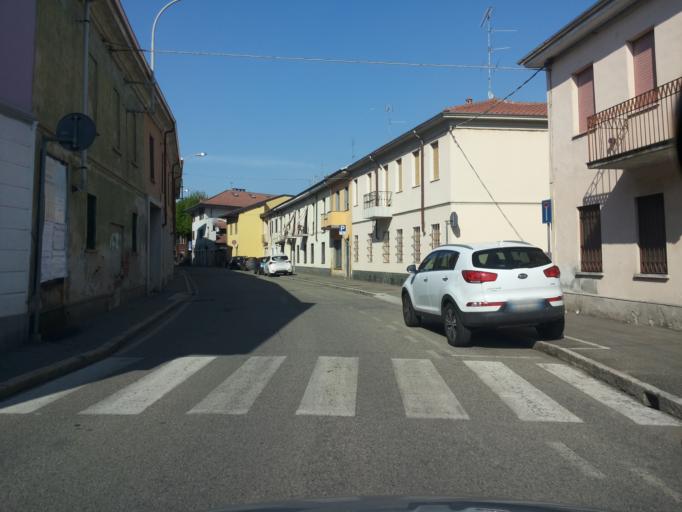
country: IT
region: Lombardy
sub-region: Provincia di Pavia
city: Cilavegna
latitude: 45.3089
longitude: 8.7417
